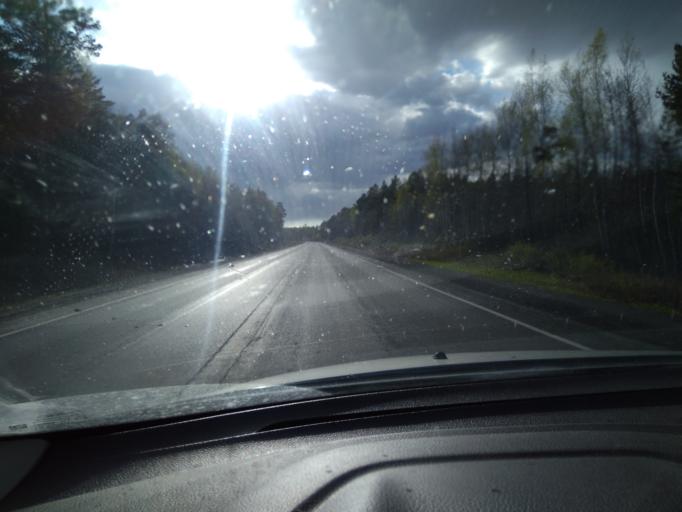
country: RU
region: Sverdlovsk
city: Yushala
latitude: 57.1126
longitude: 64.2588
